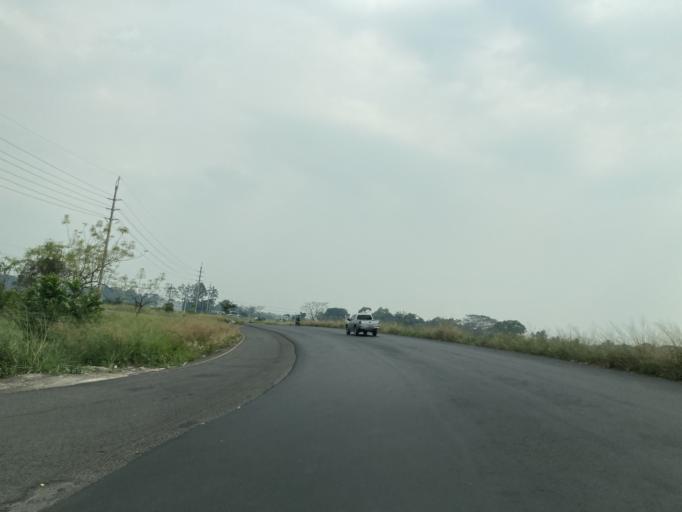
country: GT
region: Escuintla
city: Santa Lucia Cotzumalguapa
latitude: 14.3090
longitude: -91.0478
